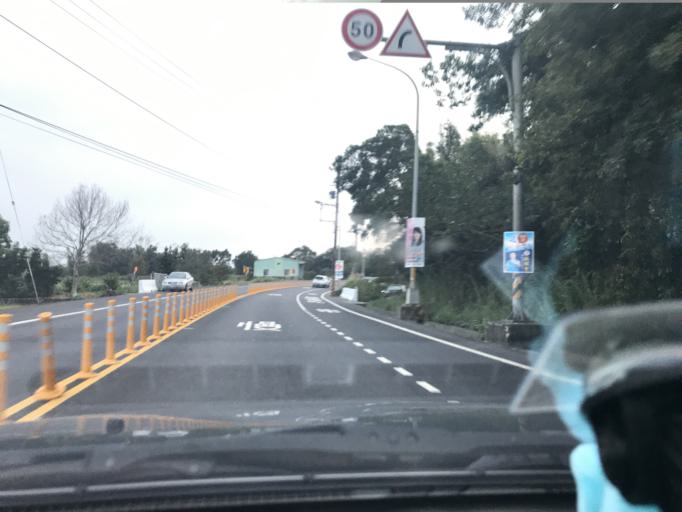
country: TW
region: Taiwan
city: Daxi
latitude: 24.8831
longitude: 121.2214
